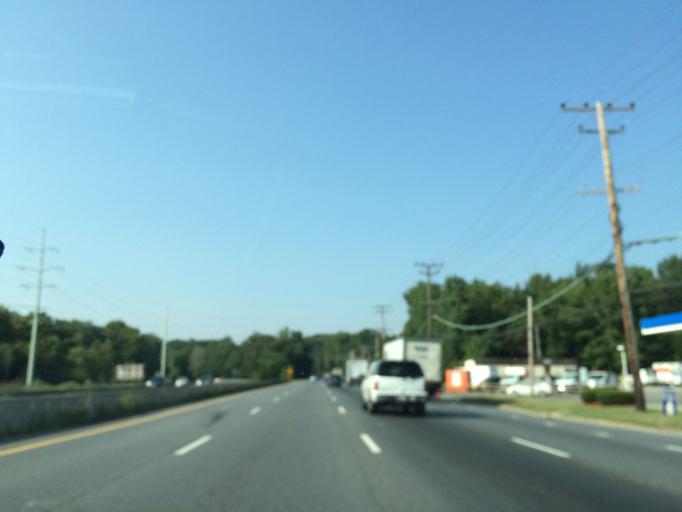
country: US
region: Maryland
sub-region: Anne Arundel County
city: Crofton
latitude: 38.9855
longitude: -76.7092
